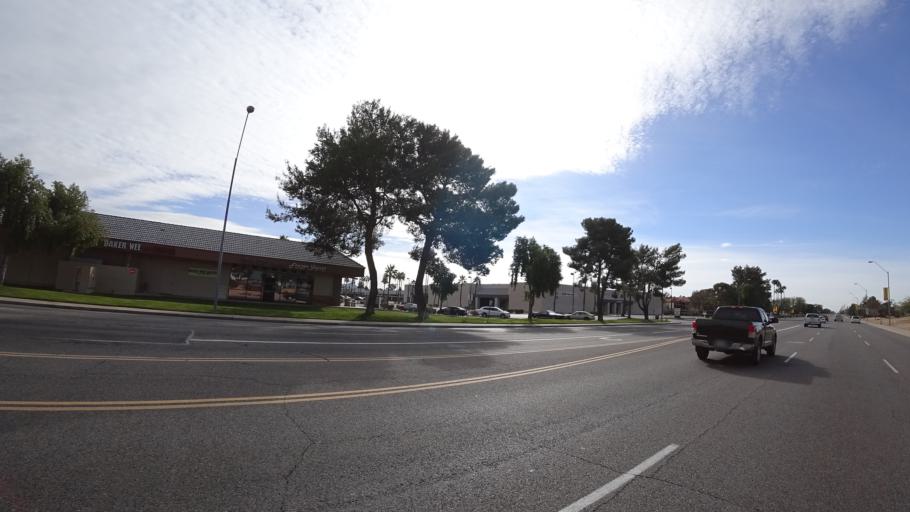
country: US
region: Arizona
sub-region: Maricopa County
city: Glendale
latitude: 33.6103
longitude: -112.1513
